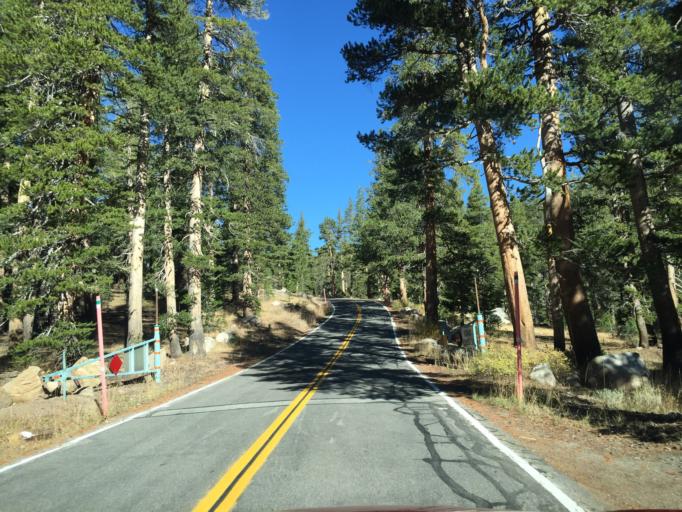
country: US
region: California
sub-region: Mono County
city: Bridgeport
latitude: 38.3091
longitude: -119.5937
